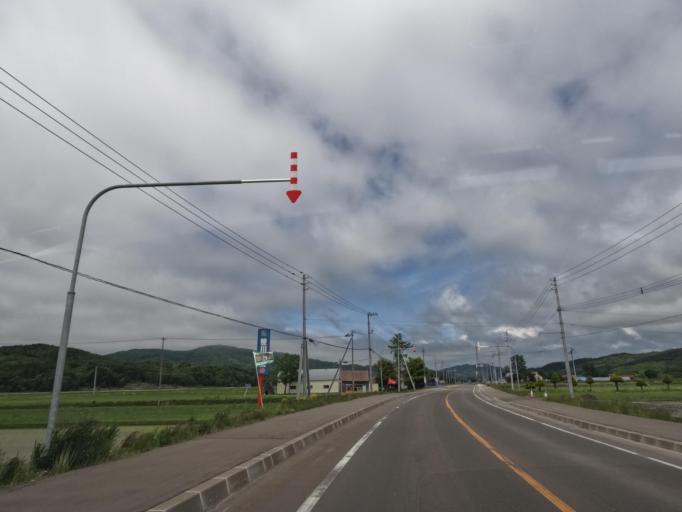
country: JP
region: Hokkaido
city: Tobetsu
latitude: 43.2684
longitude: 141.5286
